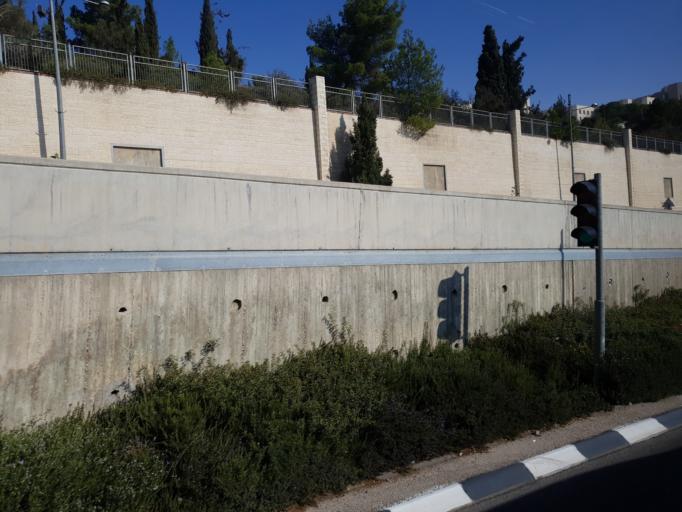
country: PS
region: West Bank
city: East Jerusalem
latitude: 31.7903
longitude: 35.2421
